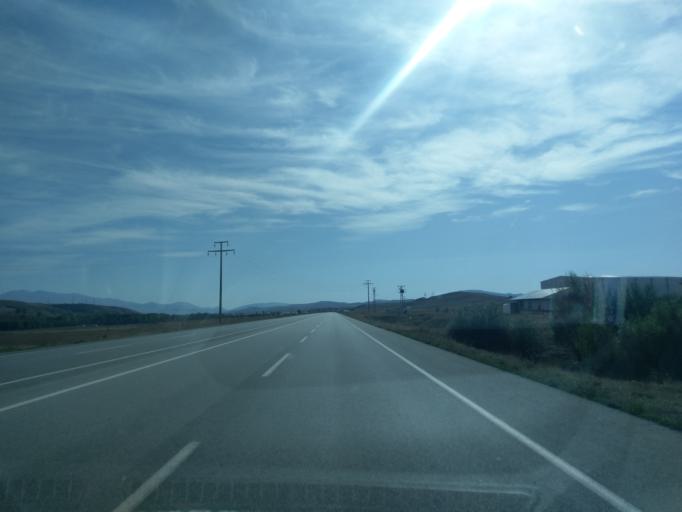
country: TR
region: Sivas
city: Imranli
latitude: 39.8741
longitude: 38.0844
